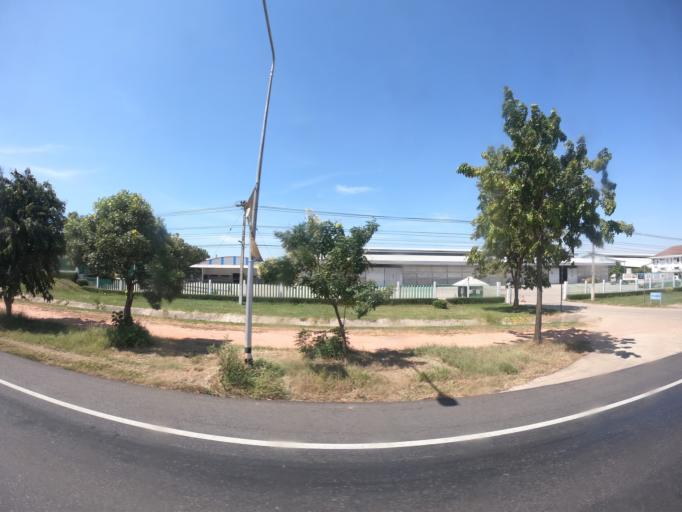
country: TH
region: Khon Kaen
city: Phon
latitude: 15.8507
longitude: 102.6190
